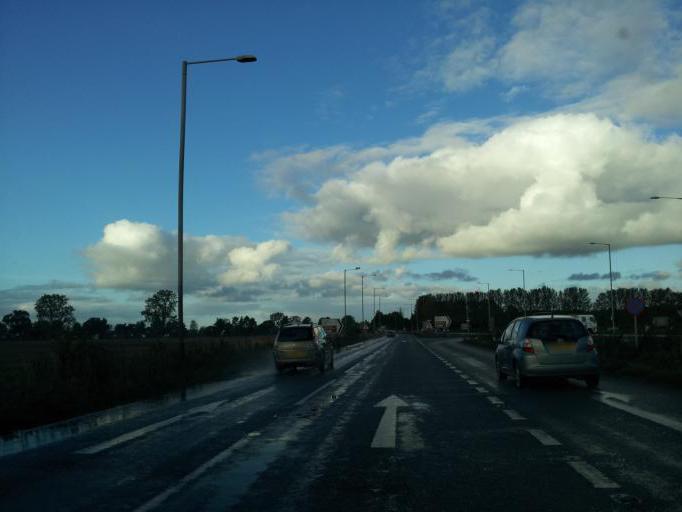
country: GB
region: England
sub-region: Norfolk
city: Lingwood
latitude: 52.6348
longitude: 1.5109
